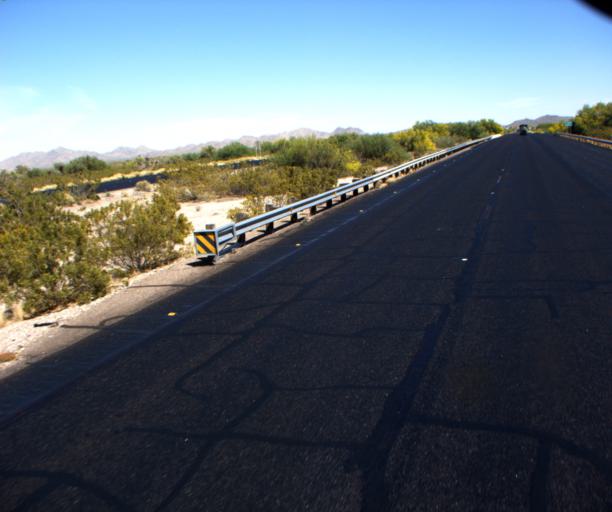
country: US
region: Arizona
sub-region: Pinal County
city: Maricopa
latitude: 32.8418
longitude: -112.2540
